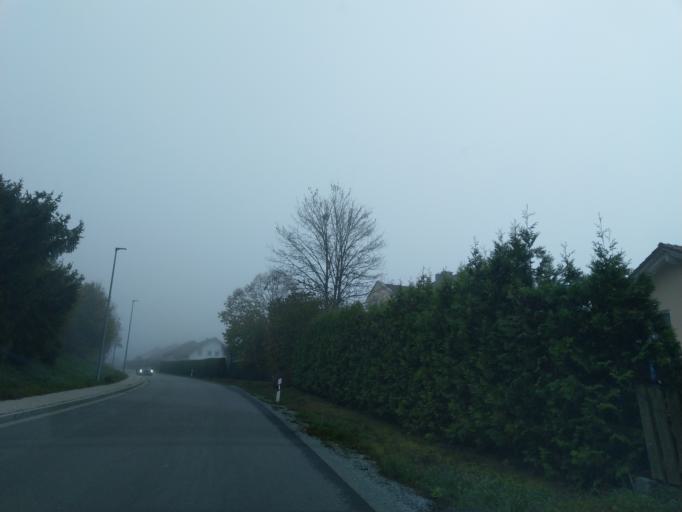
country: DE
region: Bavaria
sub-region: Lower Bavaria
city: Hengersberg
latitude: 48.7716
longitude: 13.0654
